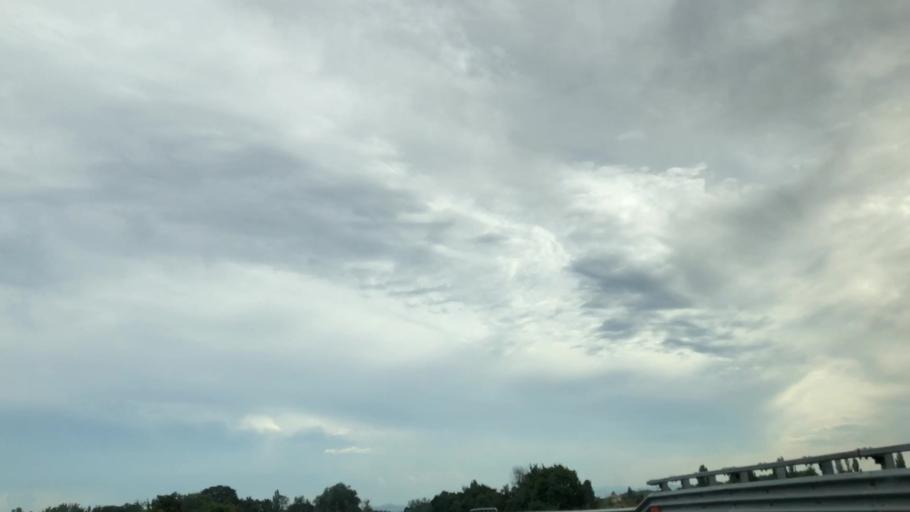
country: IT
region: Emilia-Romagna
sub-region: Provincia di Bologna
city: Bentivoglio
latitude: 44.6184
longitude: 11.4171
